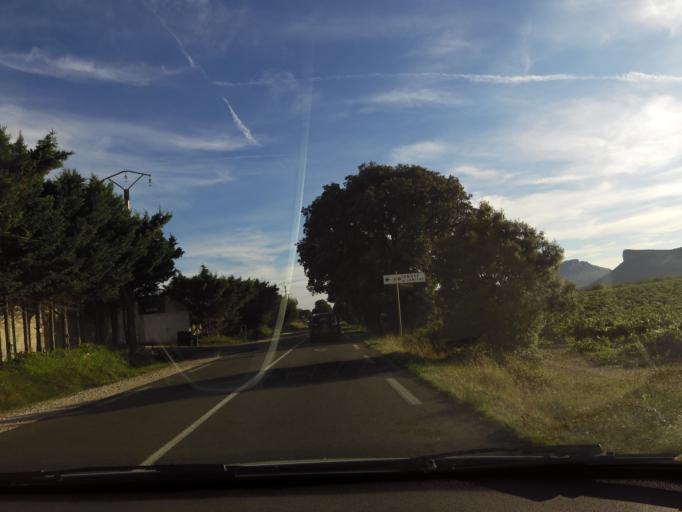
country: FR
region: Languedoc-Roussillon
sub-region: Departement de l'Herault
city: Claret
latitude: 43.8152
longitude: 3.8906
